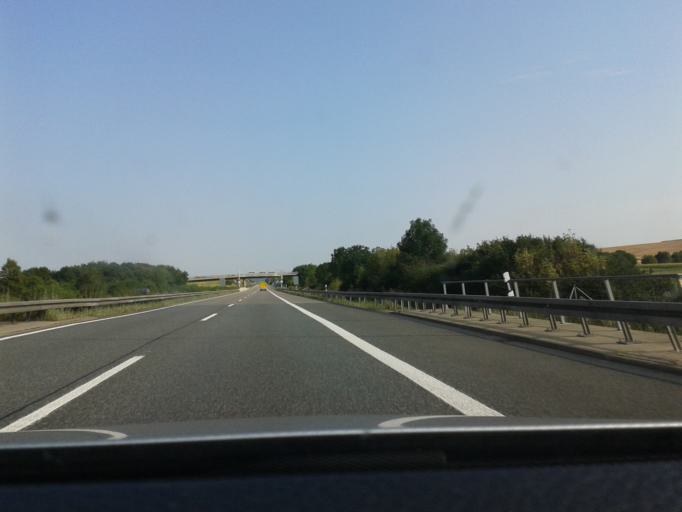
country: DE
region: Thuringia
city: Nordhausen
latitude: 51.4799
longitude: 10.7649
